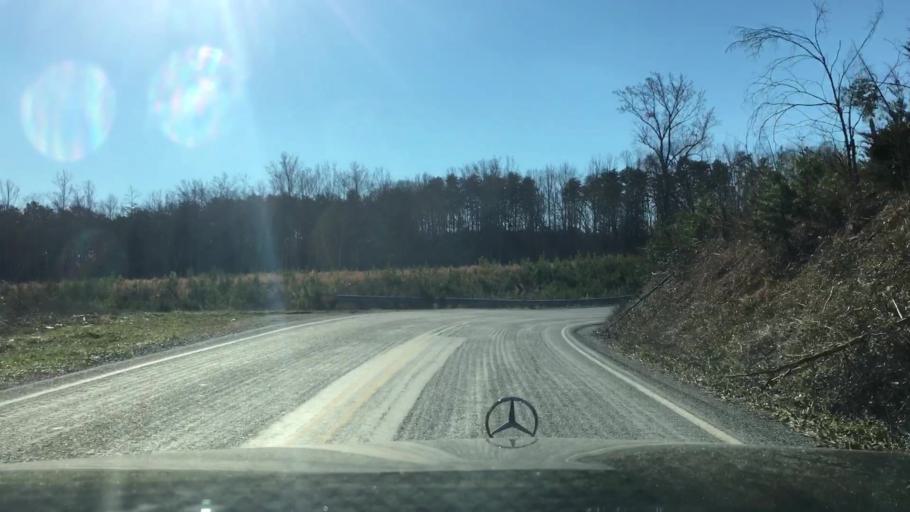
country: US
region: Virginia
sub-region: Pittsylvania County
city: Motley
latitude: 37.1537
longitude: -79.3858
